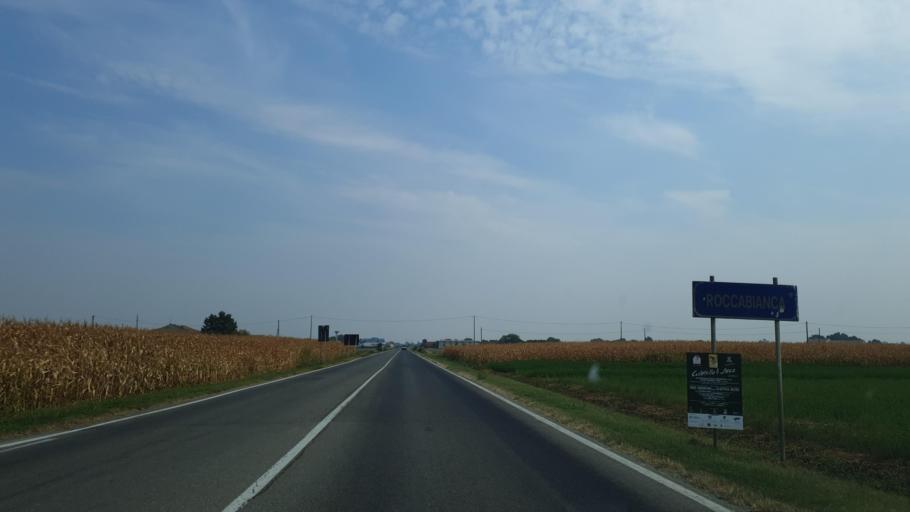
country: IT
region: Emilia-Romagna
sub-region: Provincia di Parma
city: Roccabianca
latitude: 45.0080
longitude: 10.1797
